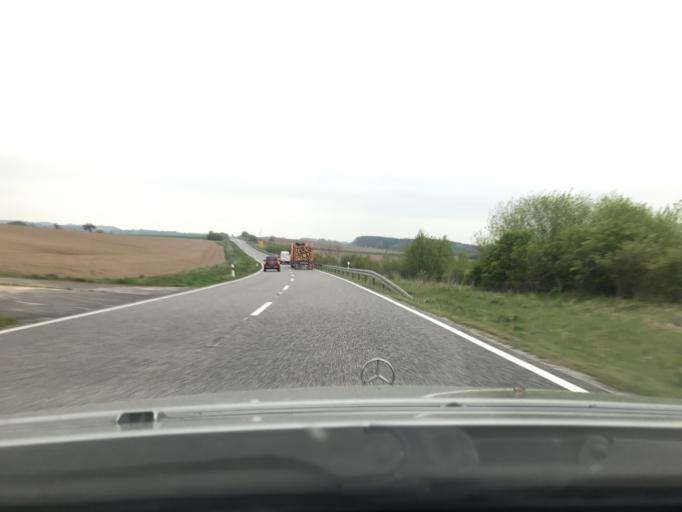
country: DE
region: Thuringia
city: Marth
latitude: 51.3856
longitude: 10.0220
